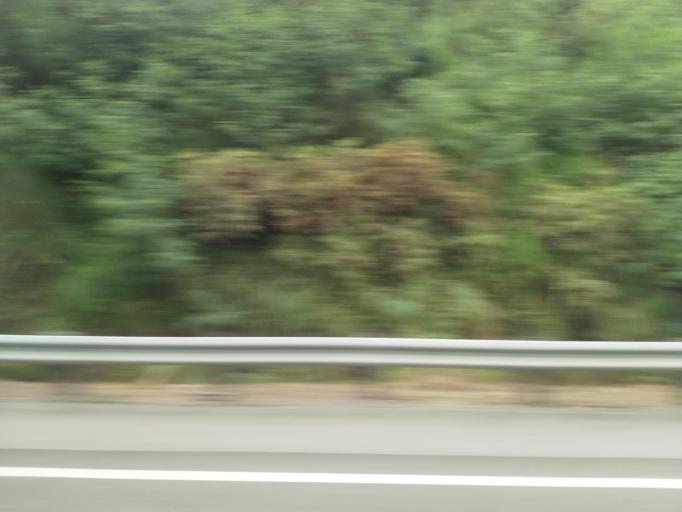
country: TW
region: Taiwan
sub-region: Pingtung
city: Pingtung
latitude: 22.7903
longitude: 120.4297
